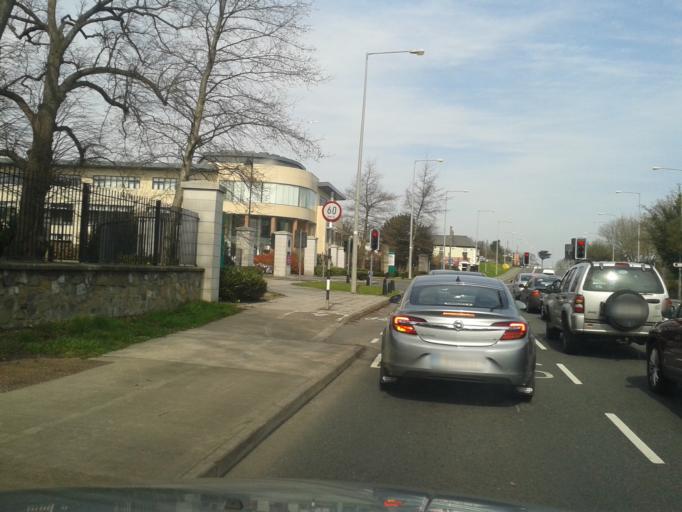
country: IE
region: Leinster
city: Beaumont
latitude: 53.4032
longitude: -6.2409
